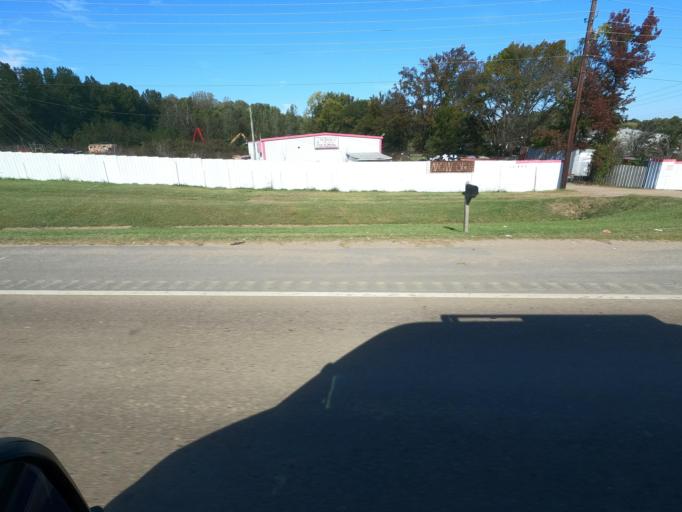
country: US
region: Tennessee
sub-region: Tipton County
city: Munford
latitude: 35.4097
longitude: -89.8344
